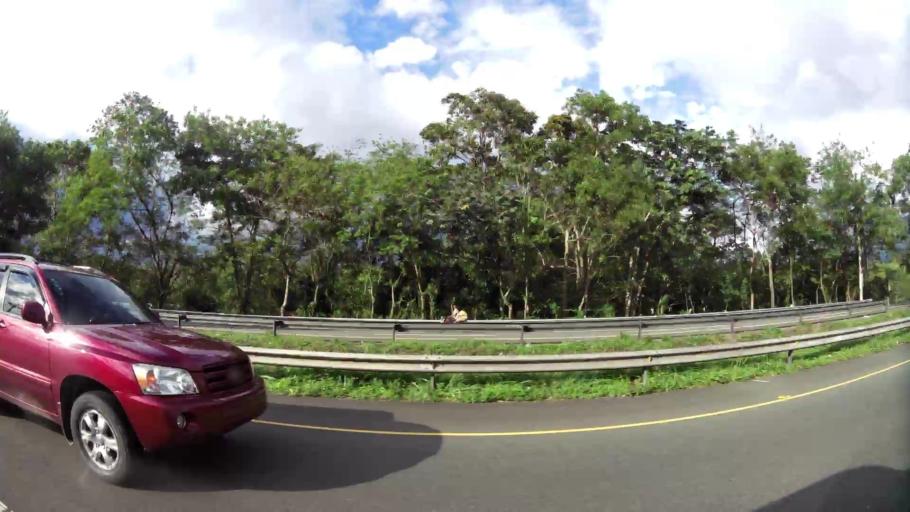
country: DO
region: Monsenor Nouel
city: Piedra Blanca
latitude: 18.8592
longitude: -70.3461
